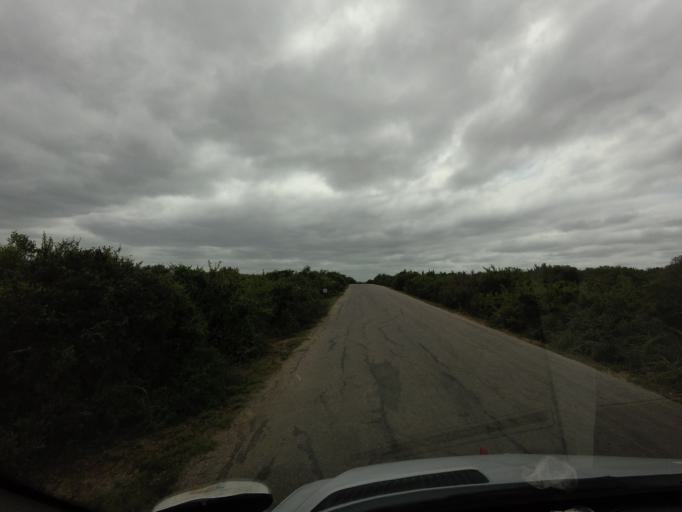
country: ZA
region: Eastern Cape
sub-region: Cacadu District Municipality
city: Kirkwood
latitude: -33.4413
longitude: 25.7514
